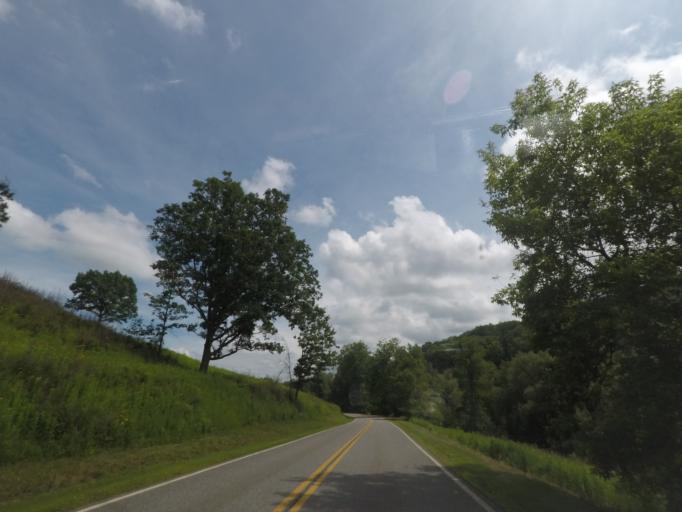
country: US
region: New York
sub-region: Saratoga County
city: Stillwater
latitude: 43.0024
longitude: -73.6120
